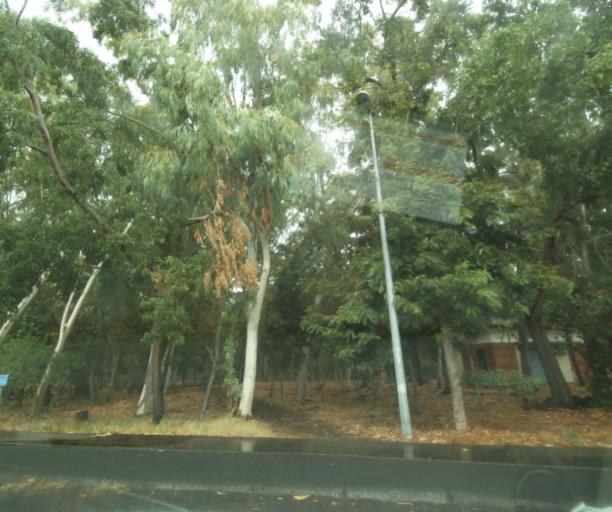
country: RE
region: Reunion
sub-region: Reunion
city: Saint-Paul
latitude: -20.9897
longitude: 55.2825
